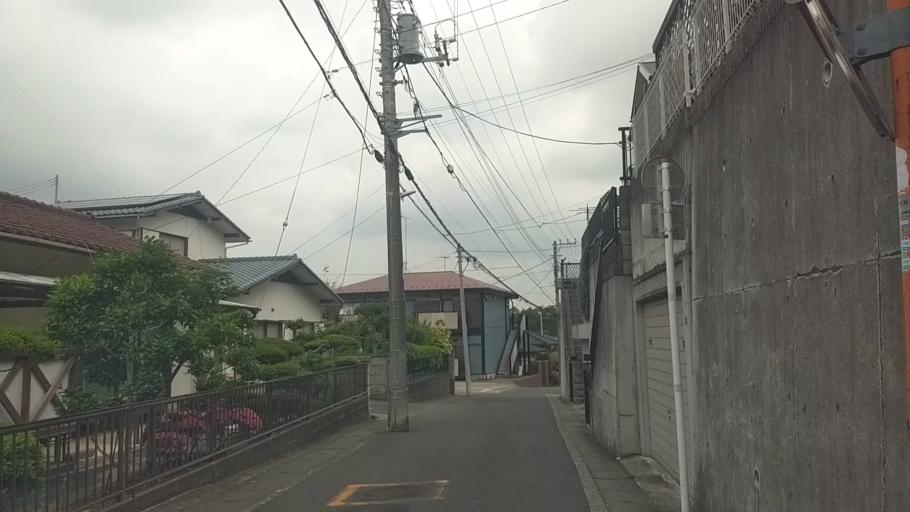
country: JP
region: Kanagawa
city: Kamakura
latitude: 35.3733
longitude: 139.5332
